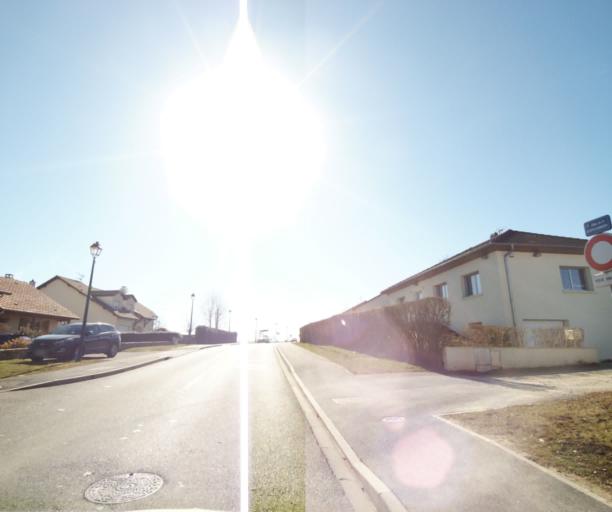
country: FR
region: Lorraine
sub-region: Departement de Meurthe-et-Moselle
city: Fleville-devant-Nancy
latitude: 48.6223
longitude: 6.2024
